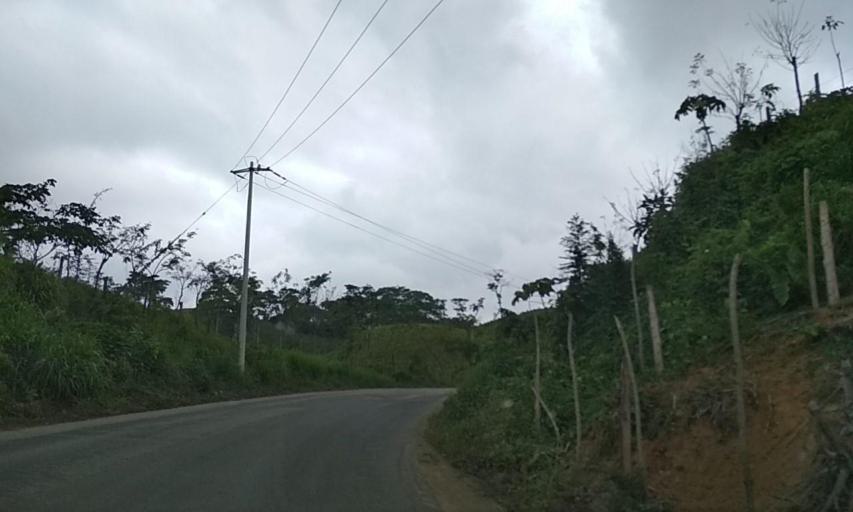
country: MX
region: Tabasco
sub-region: Huimanguillo
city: Francisco Rueda
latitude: 17.6398
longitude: -94.0929
